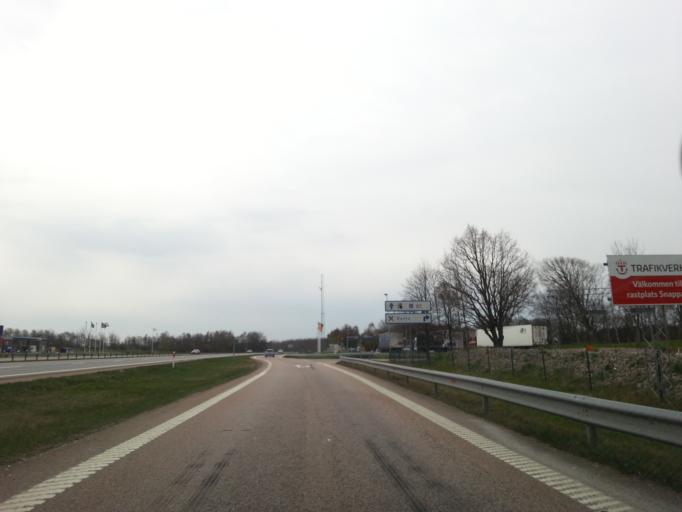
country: SE
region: Halland
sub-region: Laholms Kommun
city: Mellbystrand
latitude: 56.5427
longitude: 12.9693
